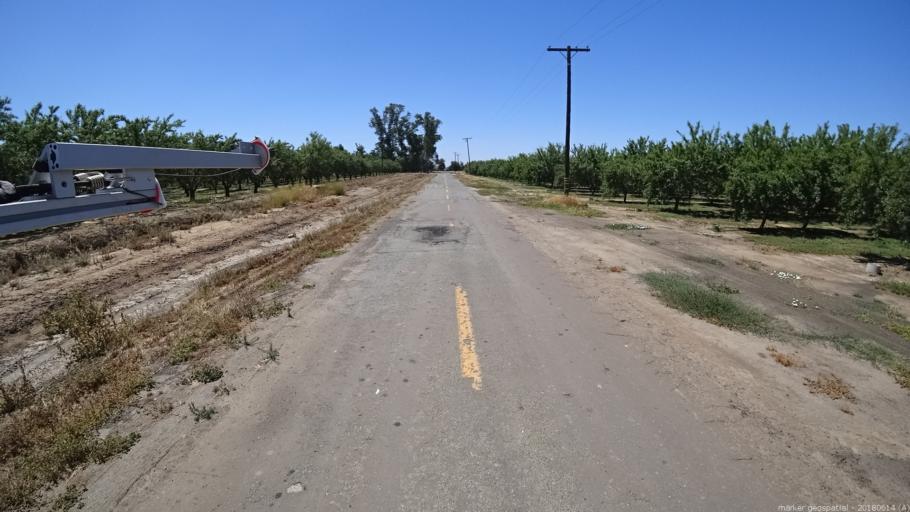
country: US
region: California
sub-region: Madera County
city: Fairmead
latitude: 37.0065
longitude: -120.2387
